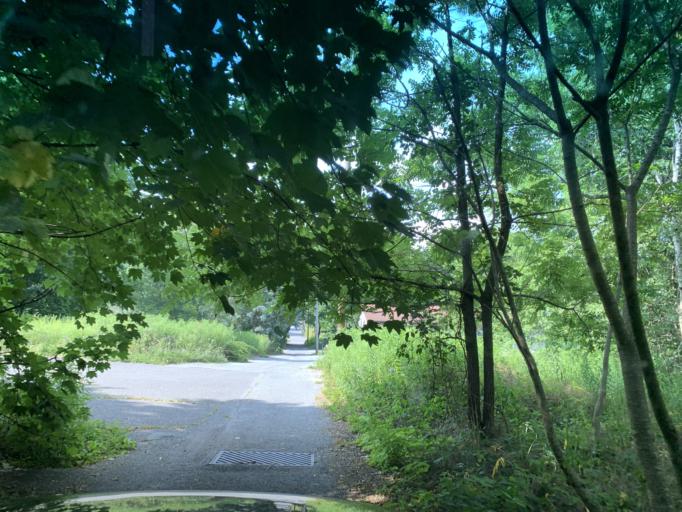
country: US
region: Pennsylvania
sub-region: Schuylkill County
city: Ashland
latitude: 40.8030
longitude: -76.3400
